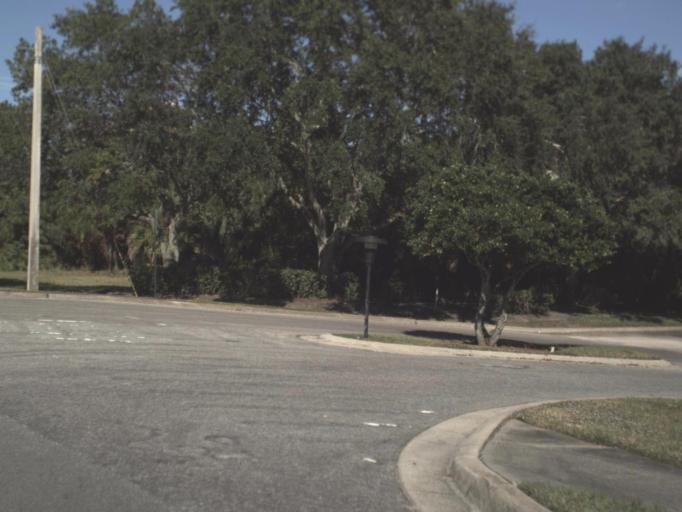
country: US
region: Florida
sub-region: Brevard County
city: South Patrick Shores
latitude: 28.2226
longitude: -80.6765
